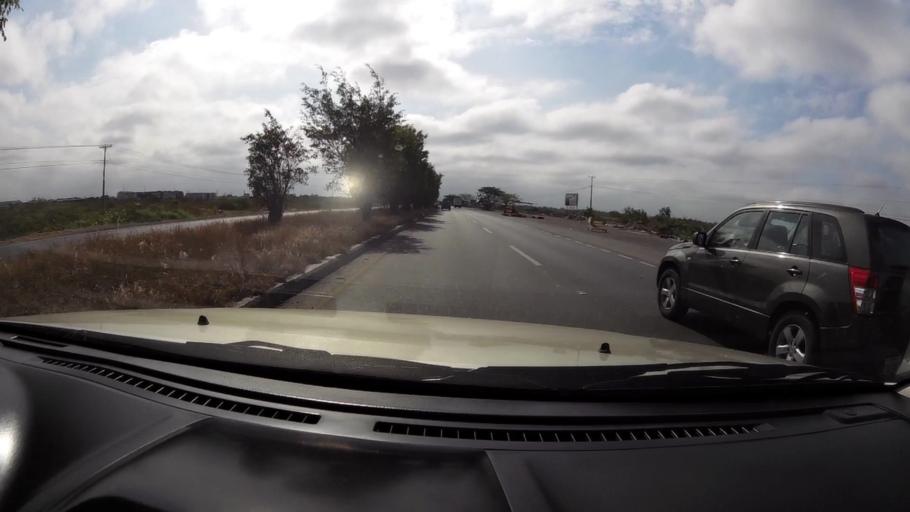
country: EC
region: Guayas
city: Eloy Alfaro
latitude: -2.1951
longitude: -79.7884
